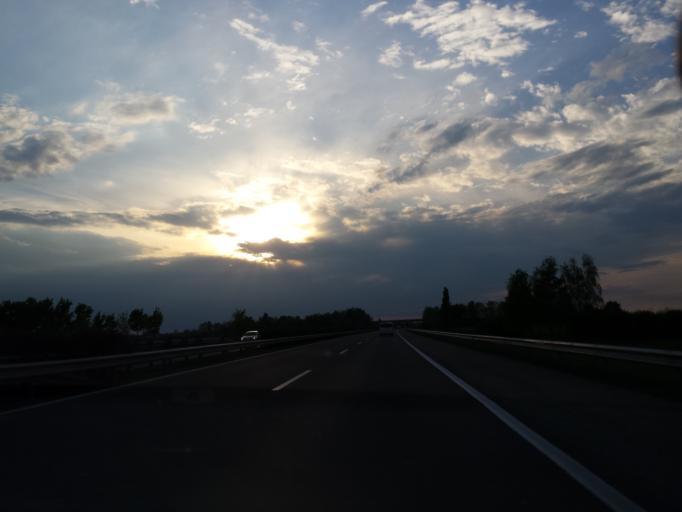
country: HU
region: Gyor-Moson-Sopron
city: Abda
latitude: 47.6910
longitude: 17.5228
